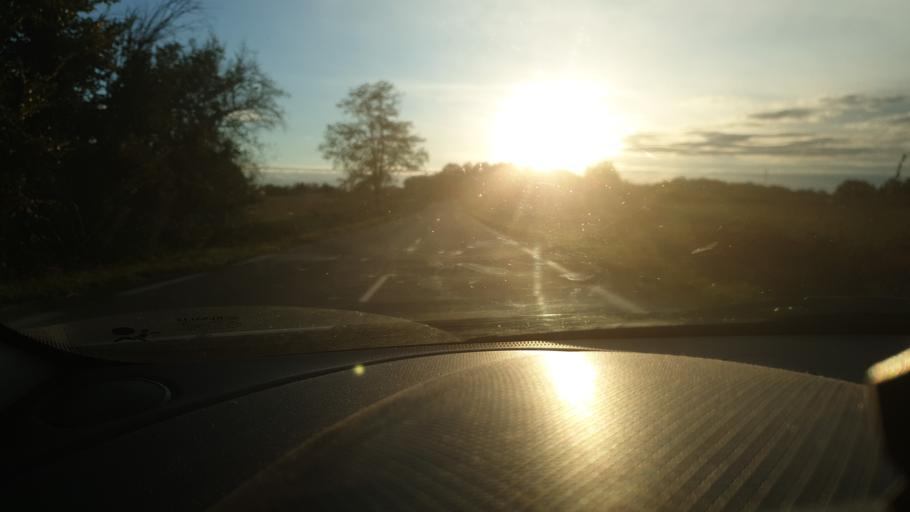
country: FR
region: Midi-Pyrenees
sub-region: Departement du Lot
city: Montcuq
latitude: 44.4025
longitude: 1.2393
